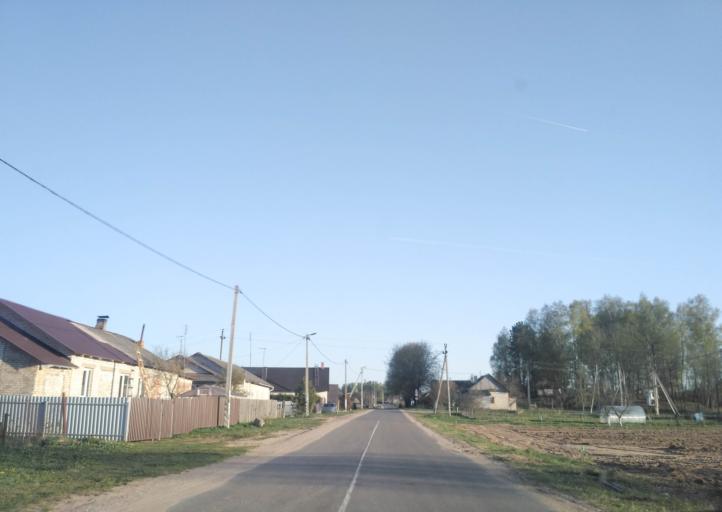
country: BY
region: Minsk
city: Pyatryshki
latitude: 54.1071
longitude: 27.1920
